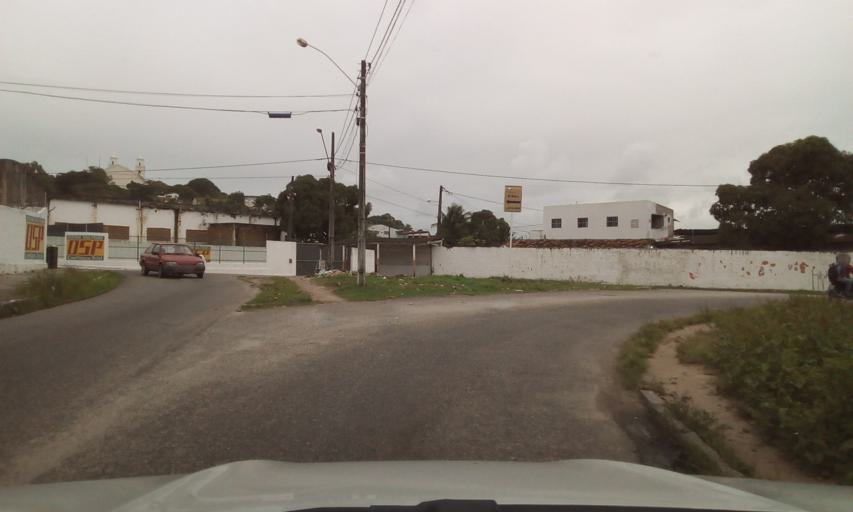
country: BR
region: Paraiba
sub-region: Joao Pessoa
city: Joao Pessoa
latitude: -7.1105
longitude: -34.8843
